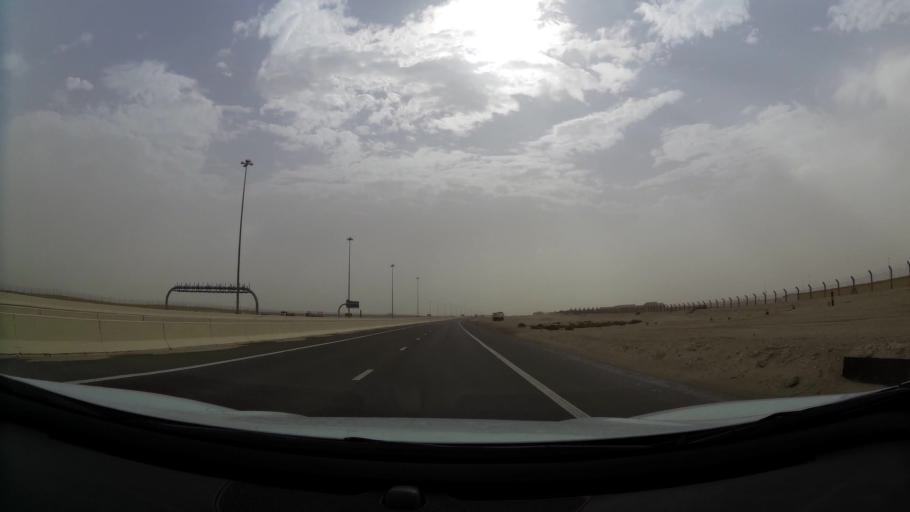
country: AE
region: Abu Dhabi
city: Abu Dhabi
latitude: 24.4800
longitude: 54.6603
